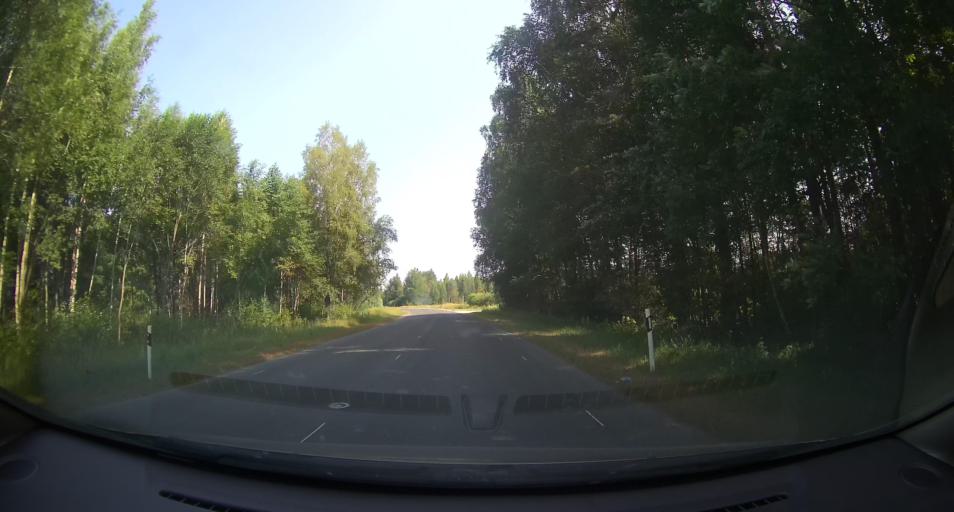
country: EE
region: Paernumaa
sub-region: Audru vald
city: Audru
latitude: 58.4523
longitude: 24.3154
